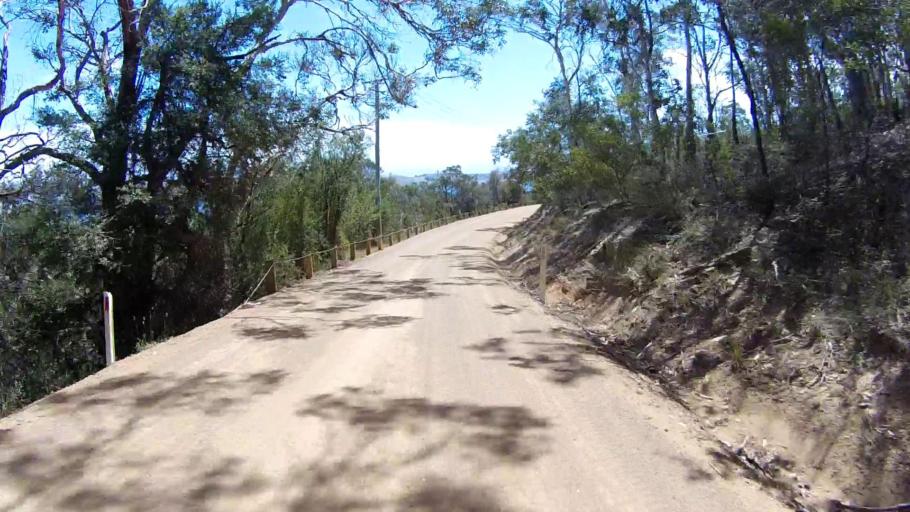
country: AU
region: Tasmania
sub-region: Clarence
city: Lauderdale
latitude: -42.9318
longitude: 147.4667
